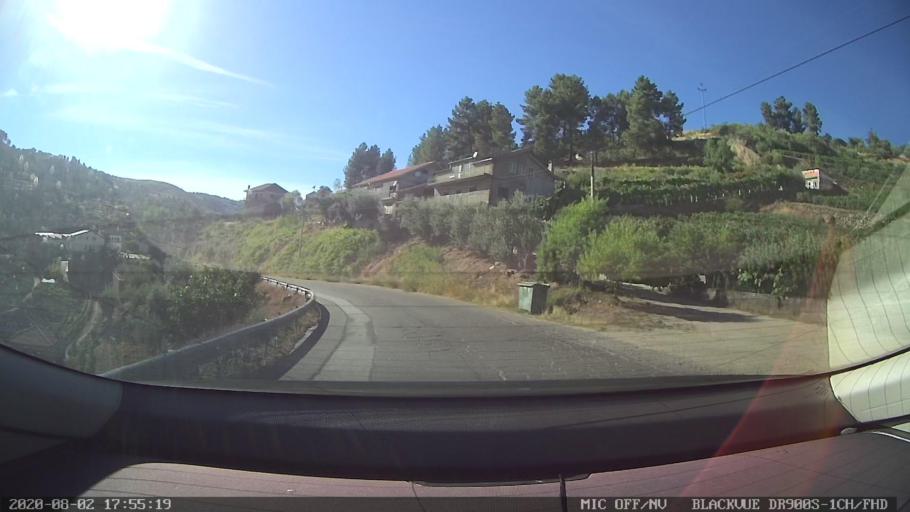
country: PT
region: Vila Real
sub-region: Murca
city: Murca
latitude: 41.4039
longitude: -7.4631
